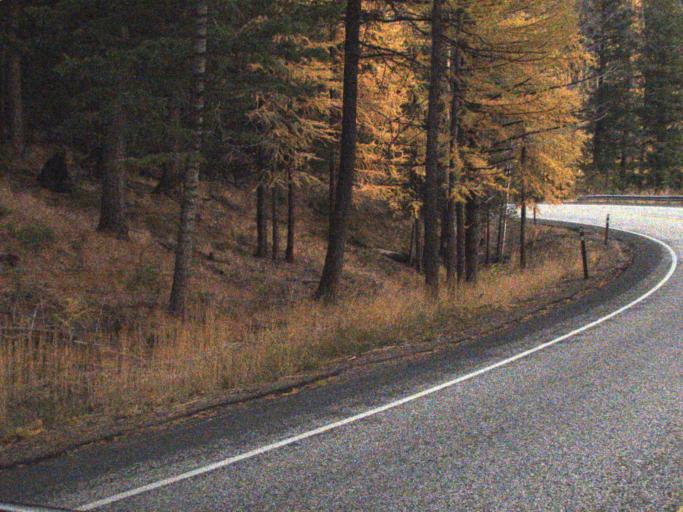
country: US
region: Washington
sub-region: Ferry County
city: Republic
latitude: 48.5993
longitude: -118.5153
